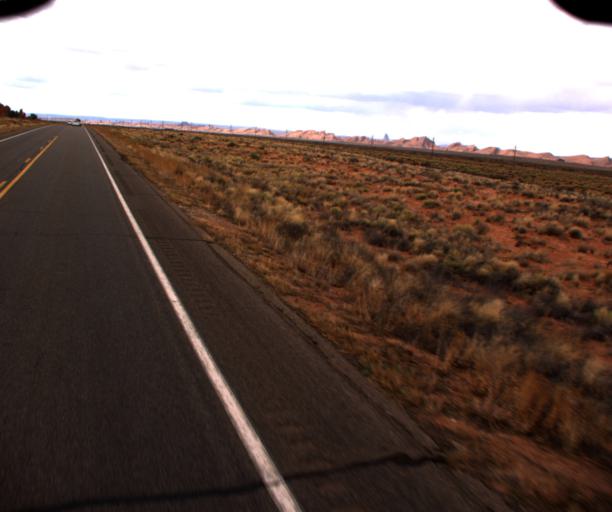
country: US
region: Arizona
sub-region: Navajo County
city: Kayenta
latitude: 36.7789
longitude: -110.0003
